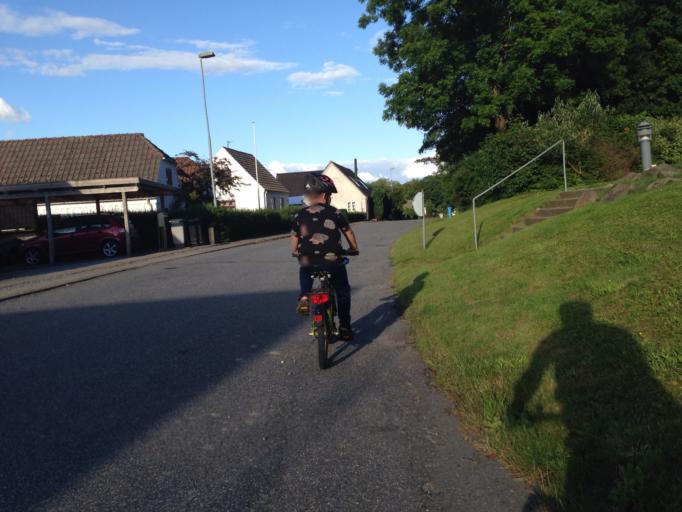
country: DK
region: South Denmark
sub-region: Middelfart Kommune
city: Norre Aby
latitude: 55.4841
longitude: 9.9052
